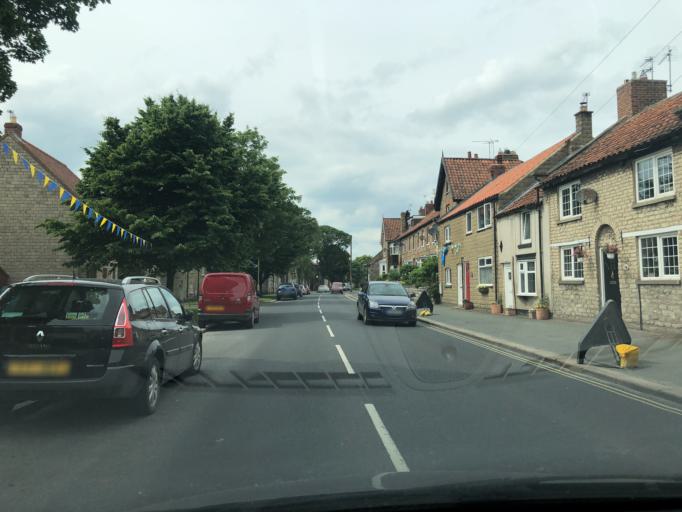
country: GB
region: England
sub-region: North Yorkshire
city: Pickering
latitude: 54.2460
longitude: -0.7853
